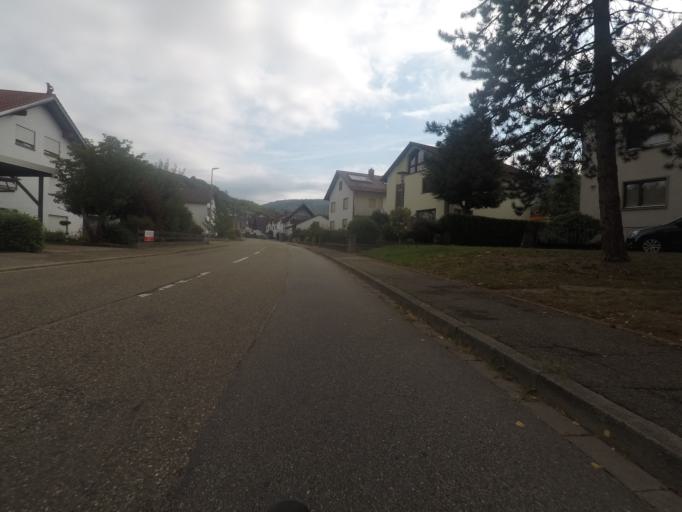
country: DE
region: Baden-Wuerttemberg
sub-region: Karlsruhe Region
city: Gaggenau
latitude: 48.8049
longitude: 8.3558
